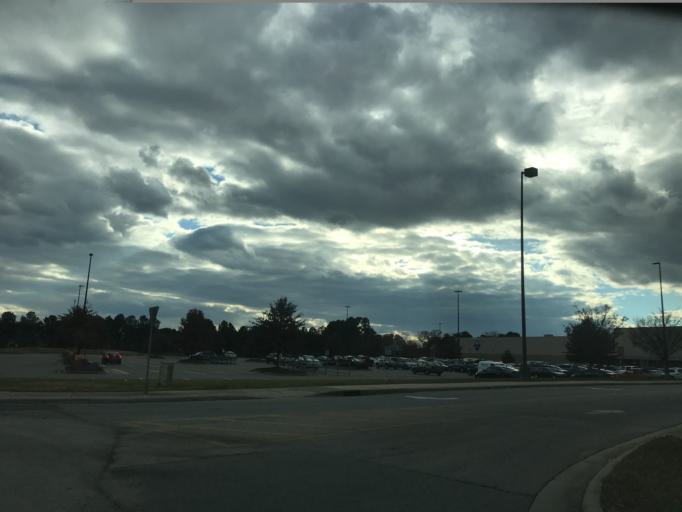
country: US
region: North Carolina
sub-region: Wake County
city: Raleigh
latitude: 35.8475
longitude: -78.5833
